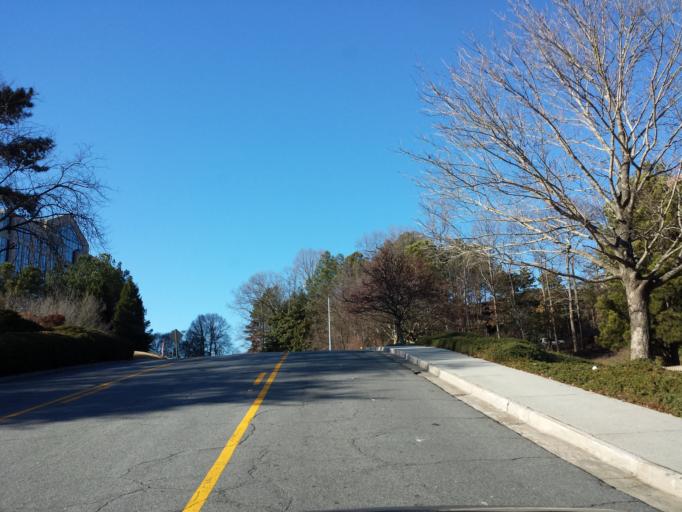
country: US
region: Georgia
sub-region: Cobb County
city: Vinings
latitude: 33.9003
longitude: -84.4599
